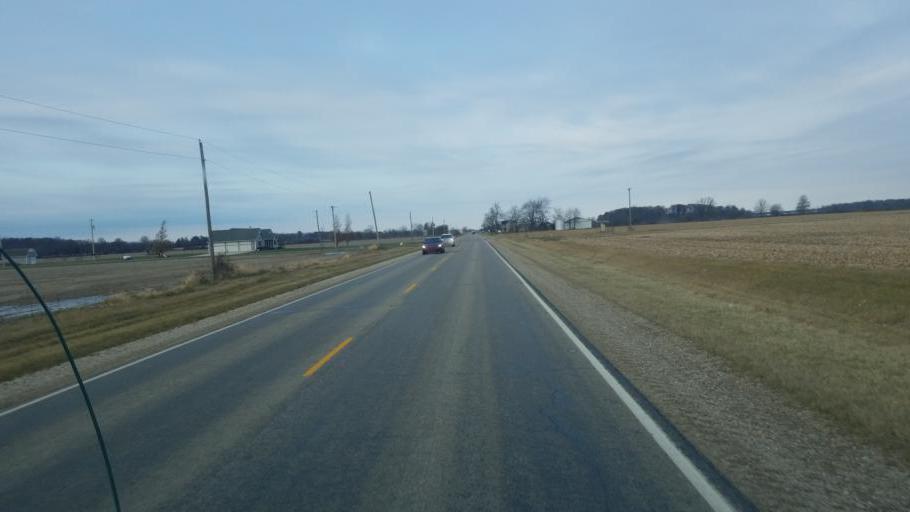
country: US
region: Indiana
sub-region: Adams County
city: Geneva
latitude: 40.5424
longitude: -84.8751
